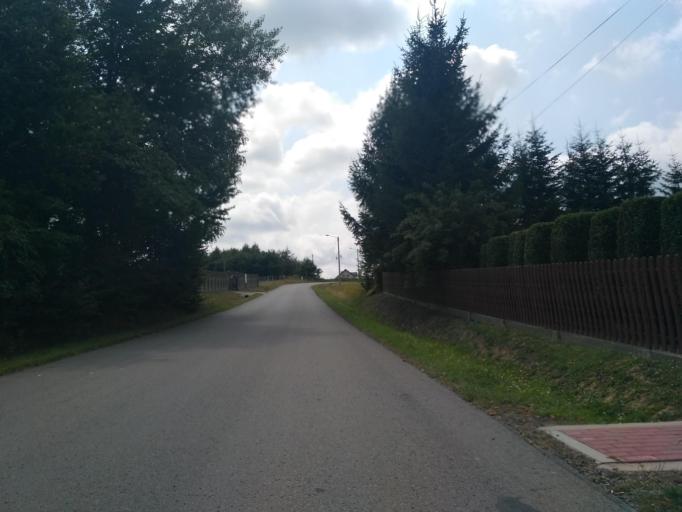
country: PL
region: Subcarpathian Voivodeship
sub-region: Powiat lancucki
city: Kraczkowa
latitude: 50.0145
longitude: 22.1597
